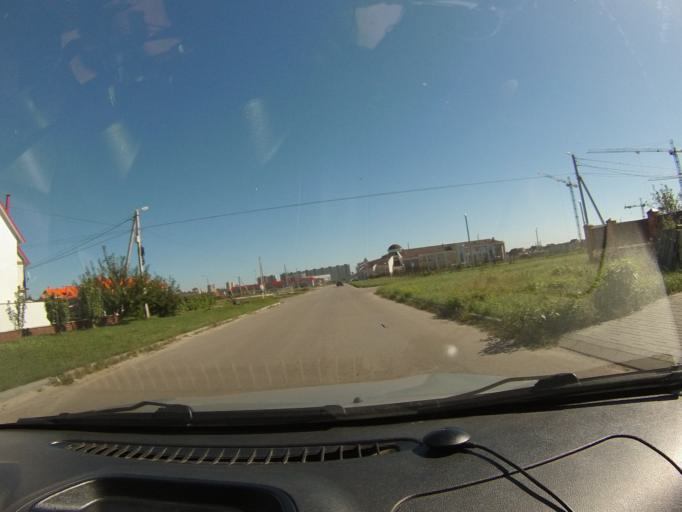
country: RU
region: Tambov
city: Tambov
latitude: 52.7718
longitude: 41.3821
